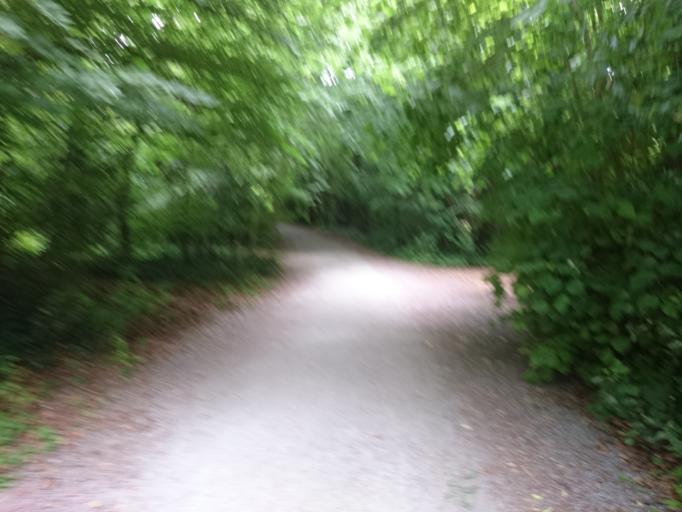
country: IE
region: Leinster
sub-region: Kilkenny
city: Kilkenny
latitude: 52.6503
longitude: -7.2404
